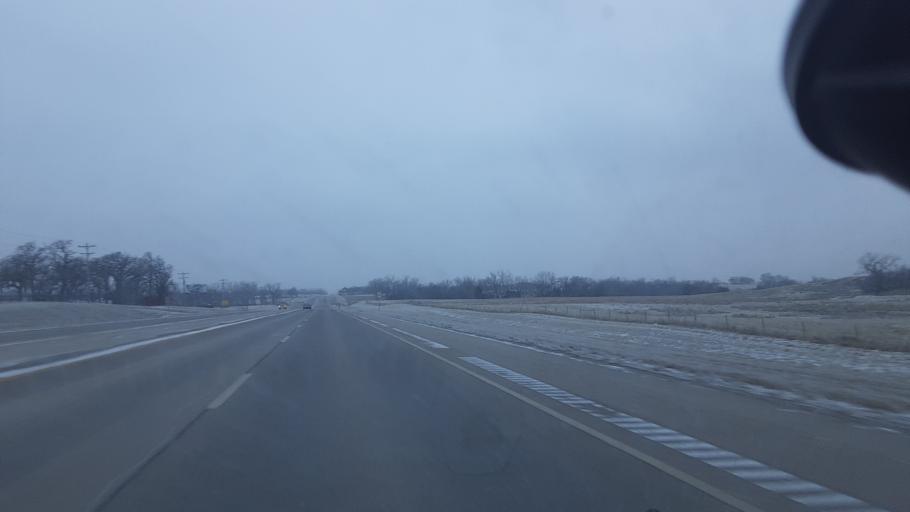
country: US
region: Oklahoma
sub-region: Payne County
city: Perkins
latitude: 35.9854
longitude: -97.0754
